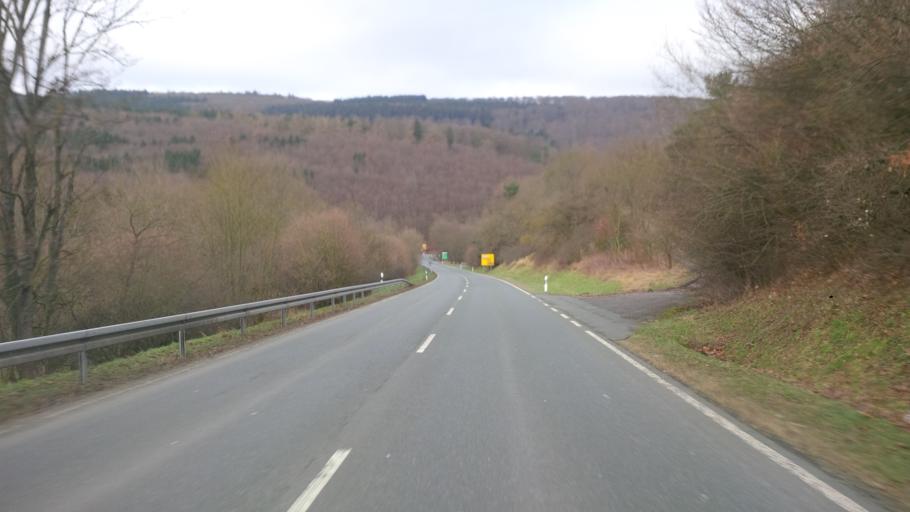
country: DE
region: Hesse
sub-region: Regierungsbezirk Darmstadt
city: Schmitten
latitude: 50.2849
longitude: 8.4657
